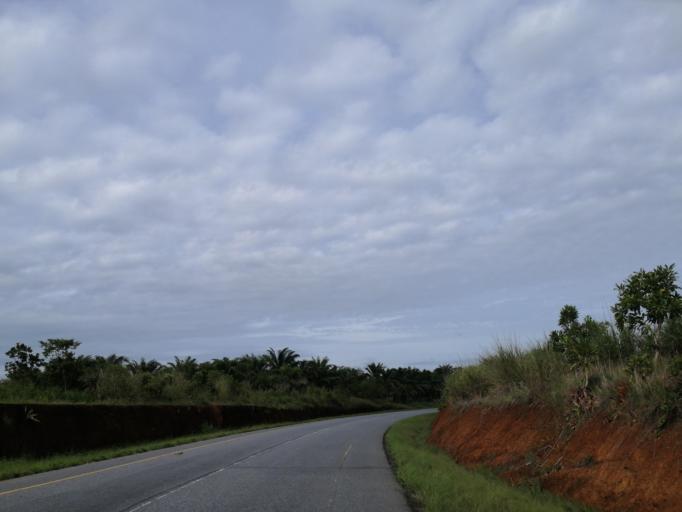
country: SL
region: Northern Province
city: Port Loko
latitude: 8.7858
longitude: -12.8484
